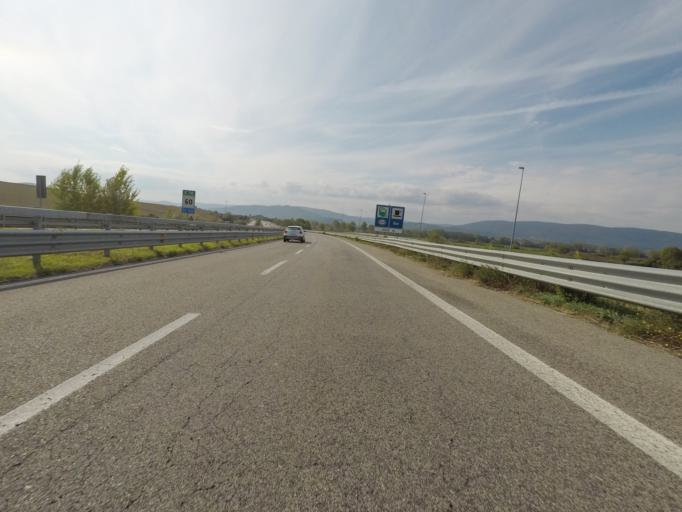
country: IT
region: Tuscany
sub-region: Provincia di Siena
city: Rosia
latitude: 43.2406
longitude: 11.2813
